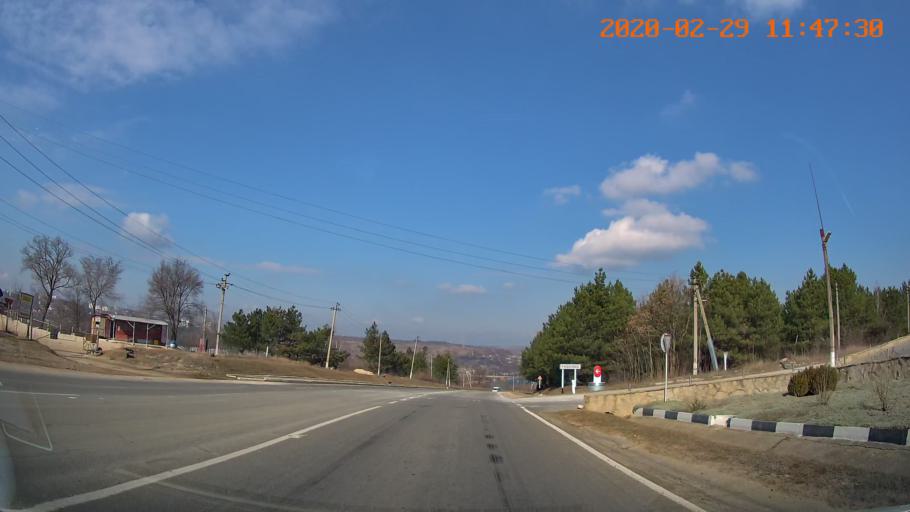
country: MD
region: Rezina
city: Rezina
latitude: 47.7412
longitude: 28.9877
